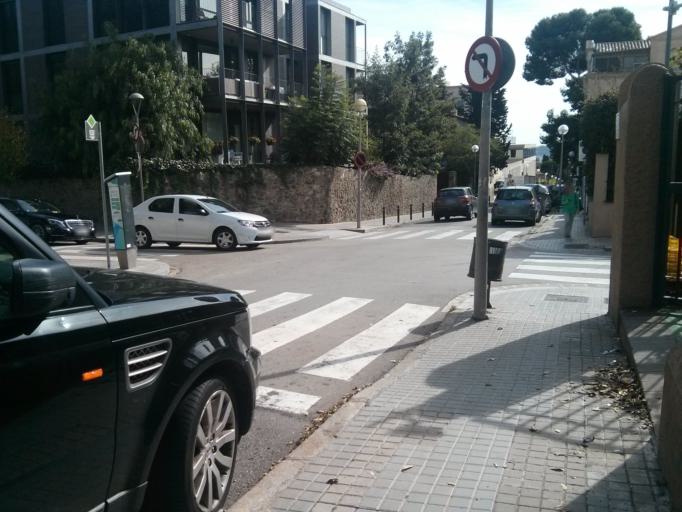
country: ES
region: Catalonia
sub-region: Provincia de Barcelona
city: Sarria-Sant Gervasi
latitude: 41.4074
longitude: 2.1253
